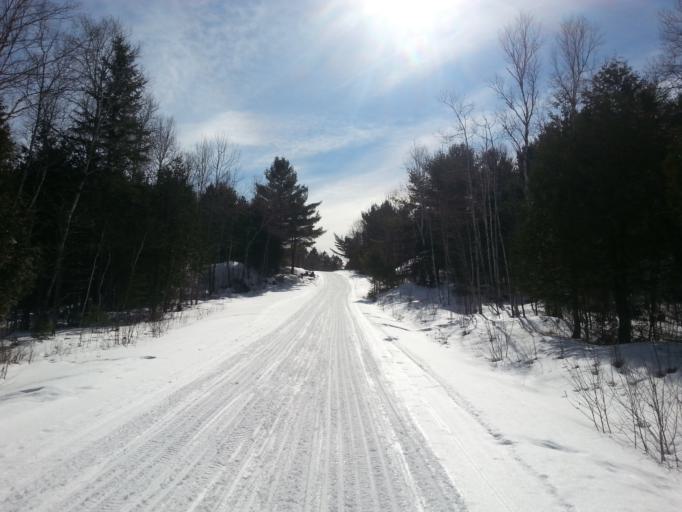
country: CA
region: Ontario
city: Greater Sudbury
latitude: 46.3385
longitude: -80.9030
